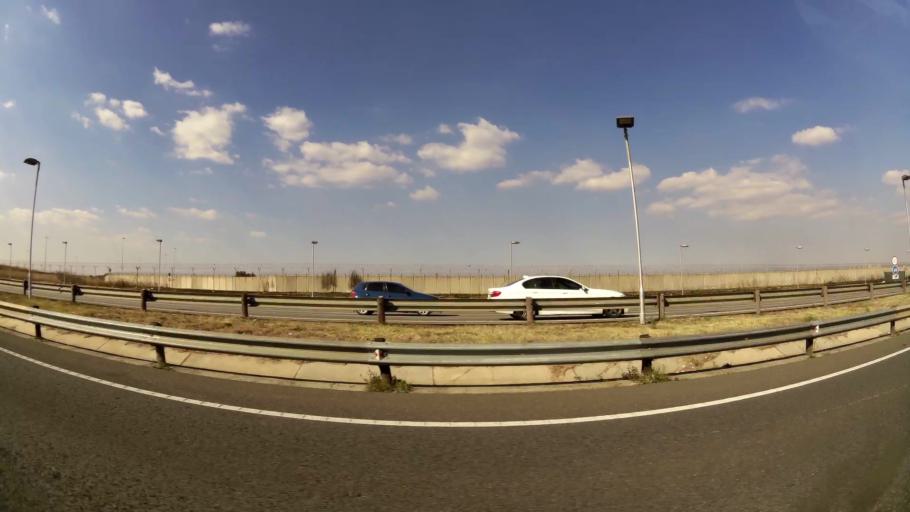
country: ZA
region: Gauteng
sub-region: City of Johannesburg Metropolitan Municipality
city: Modderfontein
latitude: -26.1032
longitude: 28.2482
